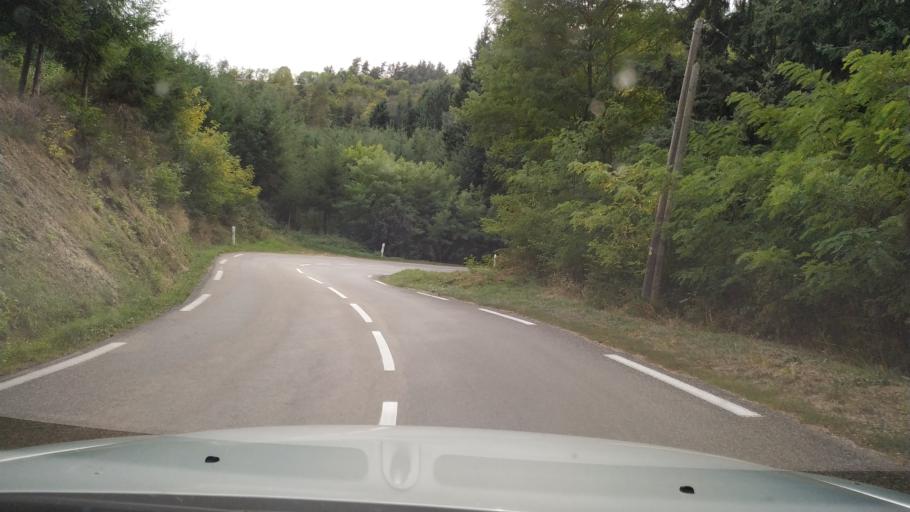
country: FR
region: Rhone-Alpes
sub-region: Departement de l'Ardeche
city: Desaignes
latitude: 44.9991
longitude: 4.5074
